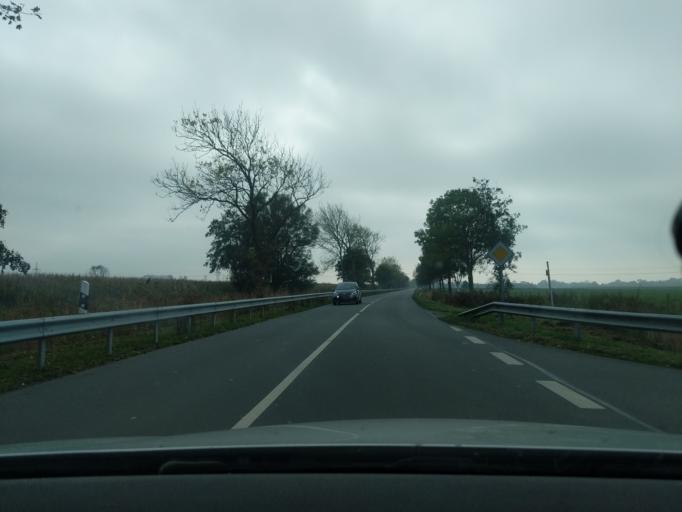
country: DE
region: Lower Saxony
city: Wanna
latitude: 53.8146
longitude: 8.7658
